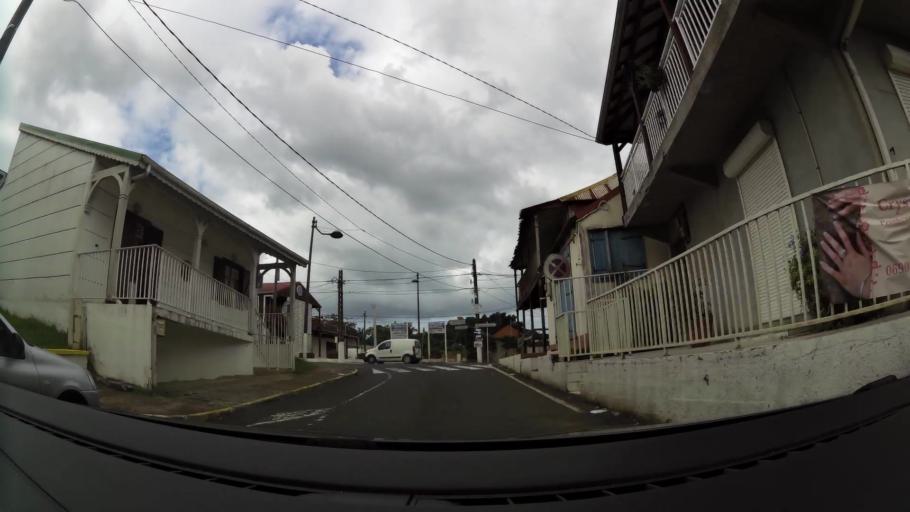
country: GP
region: Guadeloupe
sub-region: Guadeloupe
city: Lamentin
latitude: 16.2712
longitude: -61.6318
